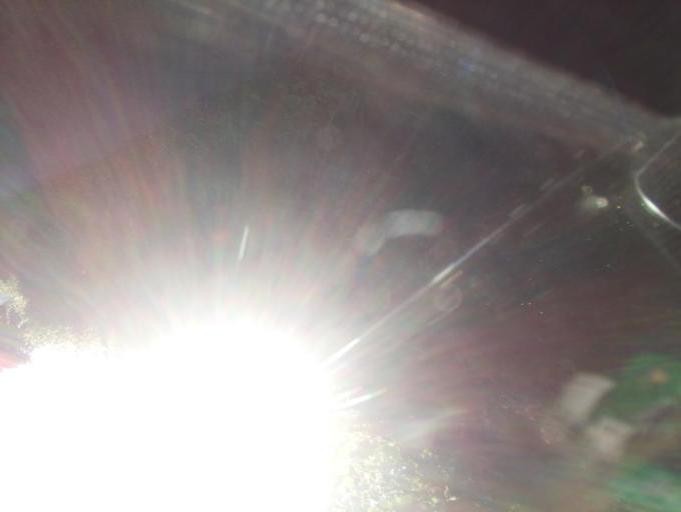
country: GB
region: Wales
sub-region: Monmouthshire
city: Tintern
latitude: 51.6843
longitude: -2.7360
